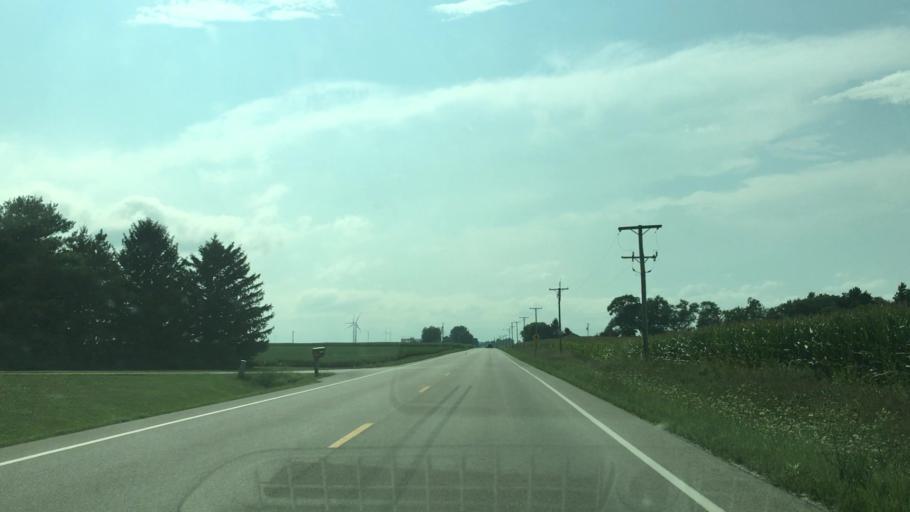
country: US
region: Illinois
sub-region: DeKalb County
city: Malta
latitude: 41.8487
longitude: -88.8437
